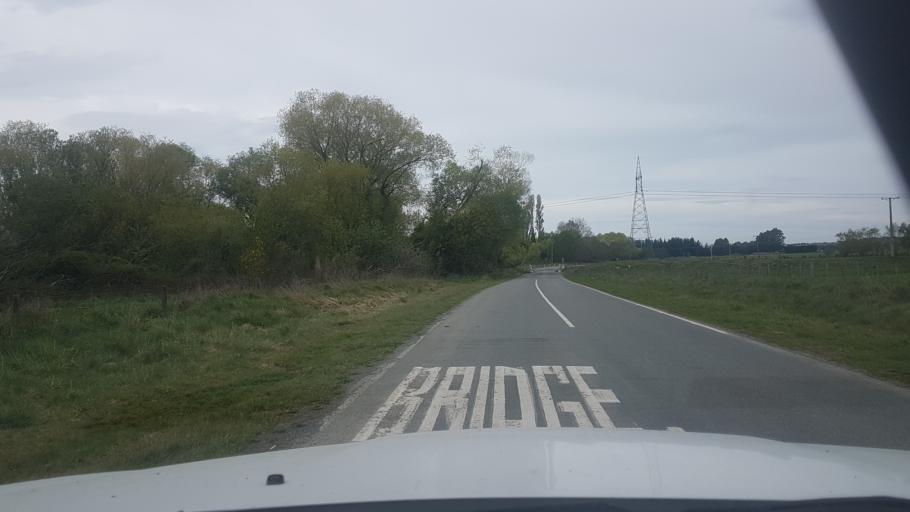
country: NZ
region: Canterbury
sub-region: Timaru District
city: Pleasant Point
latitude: -44.0661
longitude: 171.1386
